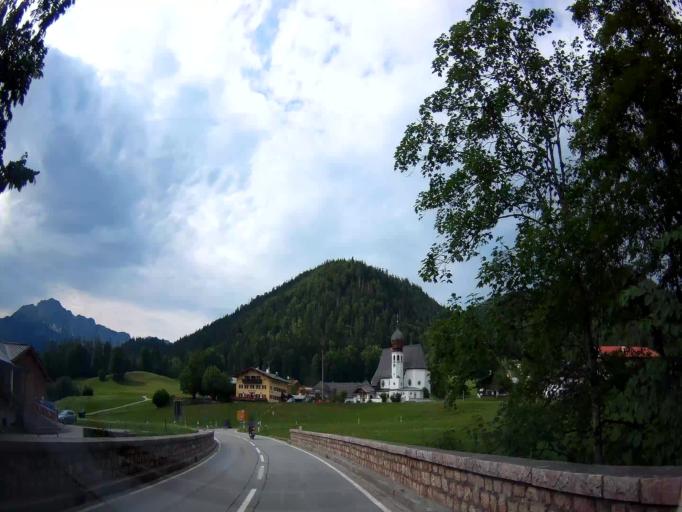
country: DE
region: Bavaria
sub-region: Upper Bavaria
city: Marktschellenberg
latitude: 47.6504
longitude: 13.0594
